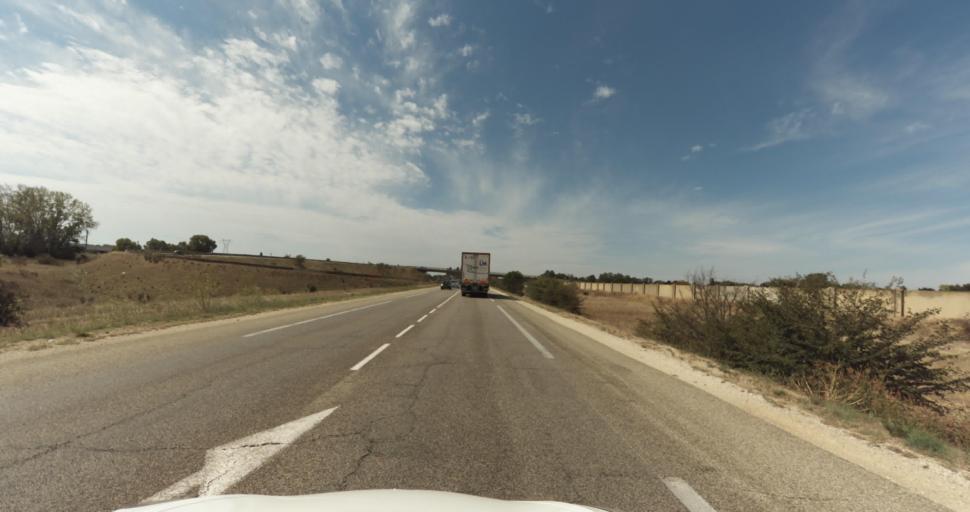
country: FR
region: Provence-Alpes-Cote d'Azur
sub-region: Departement des Bouches-du-Rhone
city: Istres
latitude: 43.5597
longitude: 4.9674
